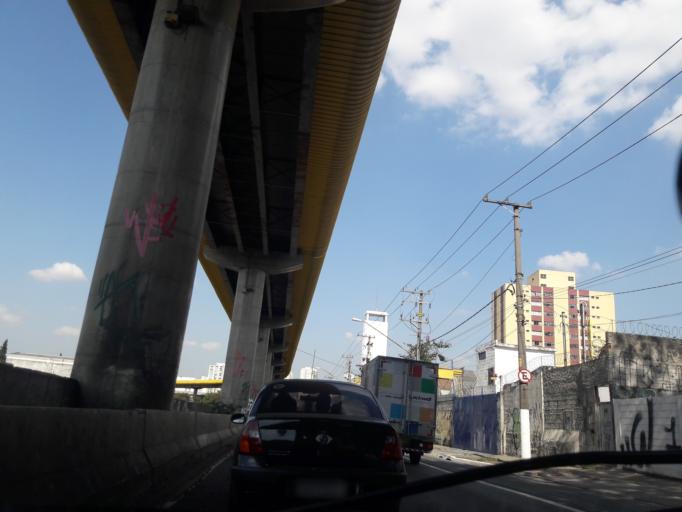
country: BR
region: Sao Paulo
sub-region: Sao Paulo
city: Sao Paulo
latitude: -23.5663
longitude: -46.6101
